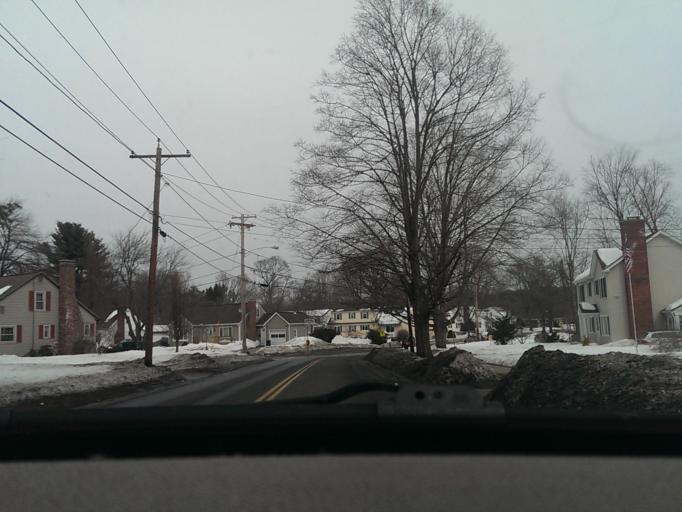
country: US
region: Massachusetts
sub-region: Hampden County
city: East Longmeadow
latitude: 42.0736
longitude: -72.5128
